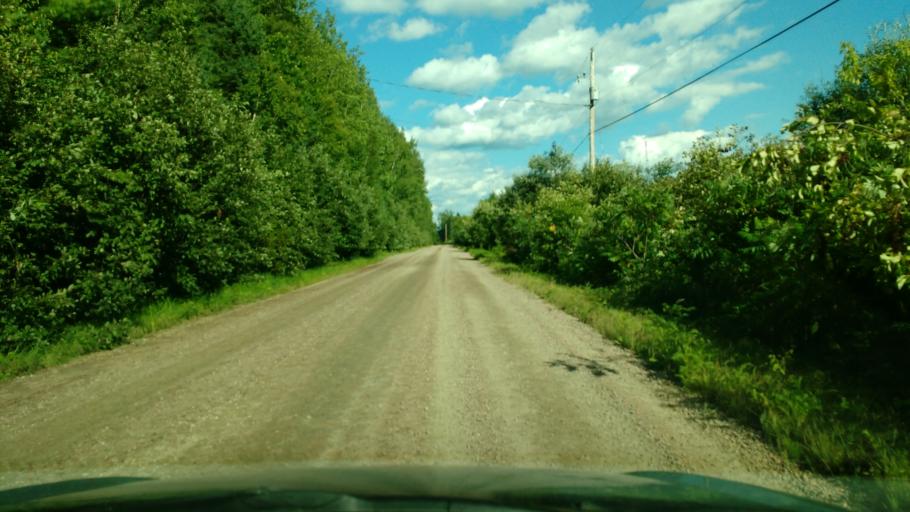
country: CA
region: Ontario
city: Powassan
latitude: 46.1898
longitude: -79.2876
